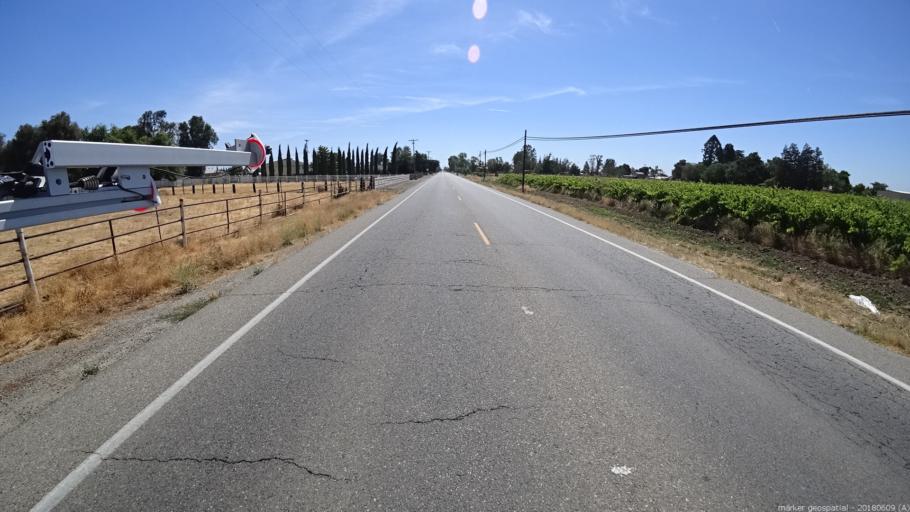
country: US
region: California
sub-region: Madera County
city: Madera
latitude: 36.9529
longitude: -120.1271
